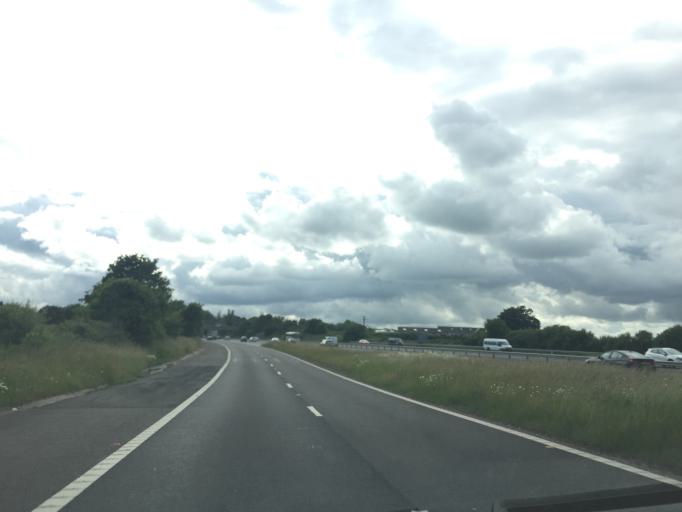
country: GB
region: England
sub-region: Hampshire
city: Totton
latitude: 50.9454
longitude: -1.5325
